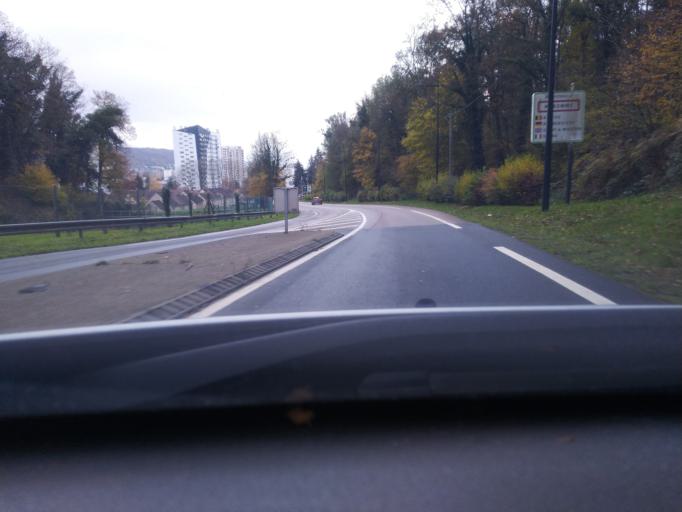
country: FR
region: Haute-Normandie
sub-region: Departement de la Seine-Maritime
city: Maromme
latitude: 49.4840
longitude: 1.0350
